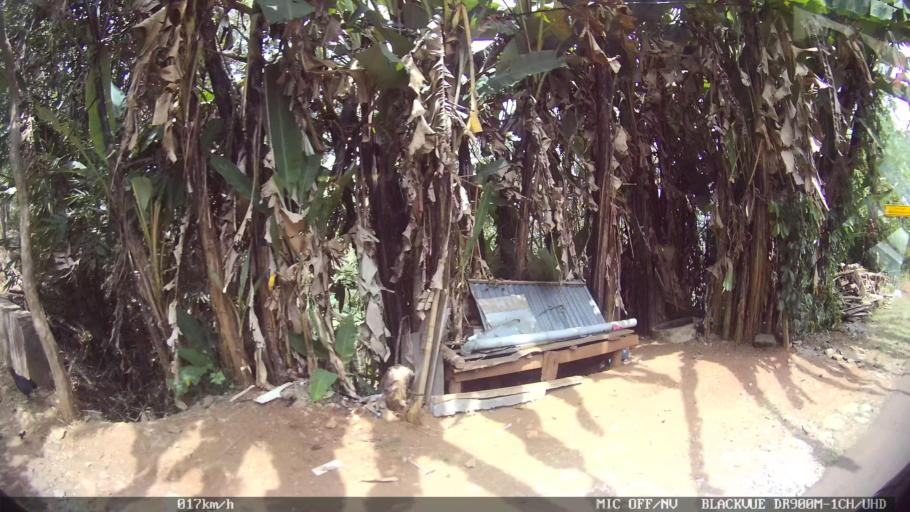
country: ID
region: Central Java
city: Candi Prambanan
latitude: -7.7947
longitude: 110.5198
